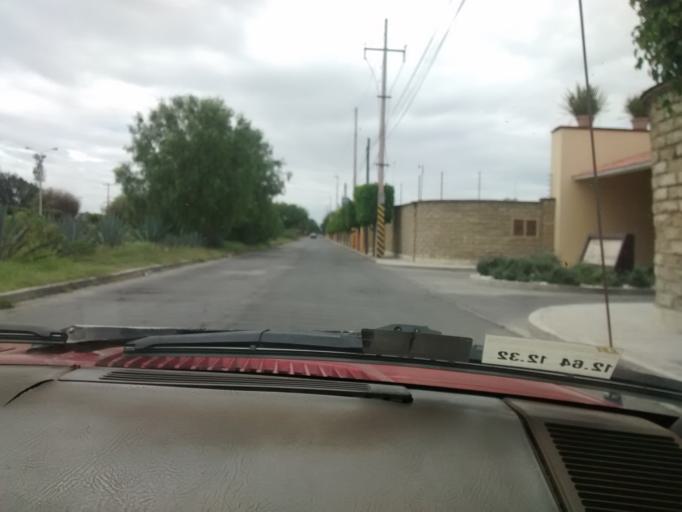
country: MX
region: Puebla
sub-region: Santiago Miahuatlan
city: San Isidro Vista Hermosa
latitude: 18.4813
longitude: -97.4125
